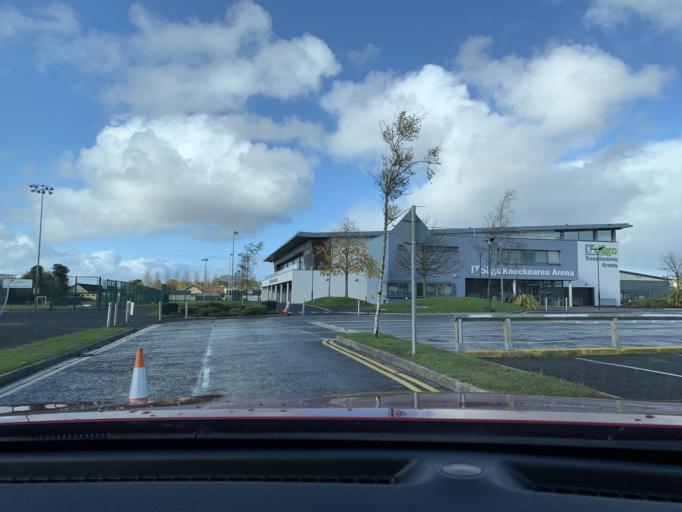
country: IE
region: Connaught
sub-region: Sligo
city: Sligo
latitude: 54.2787
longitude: -8.4645
